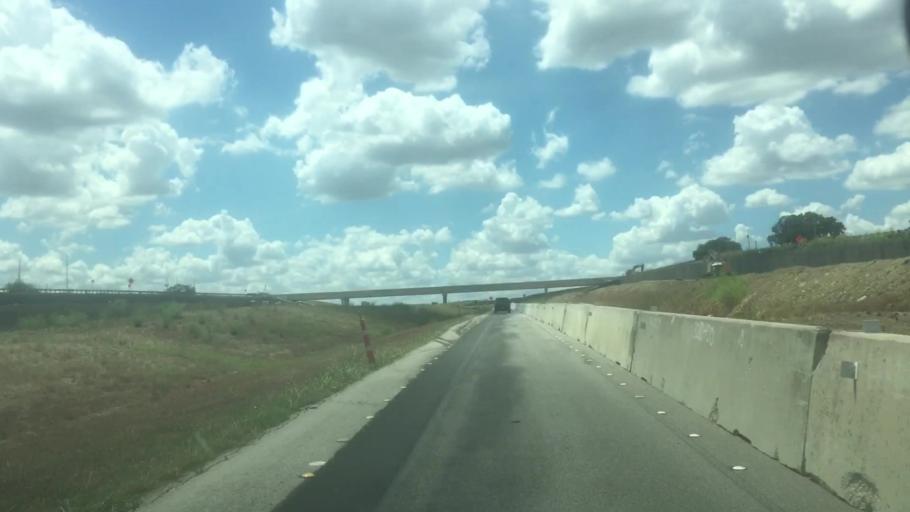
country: US
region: Texas
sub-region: Caldwell County
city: Lockhart
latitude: 29.8543
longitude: -97.7178
